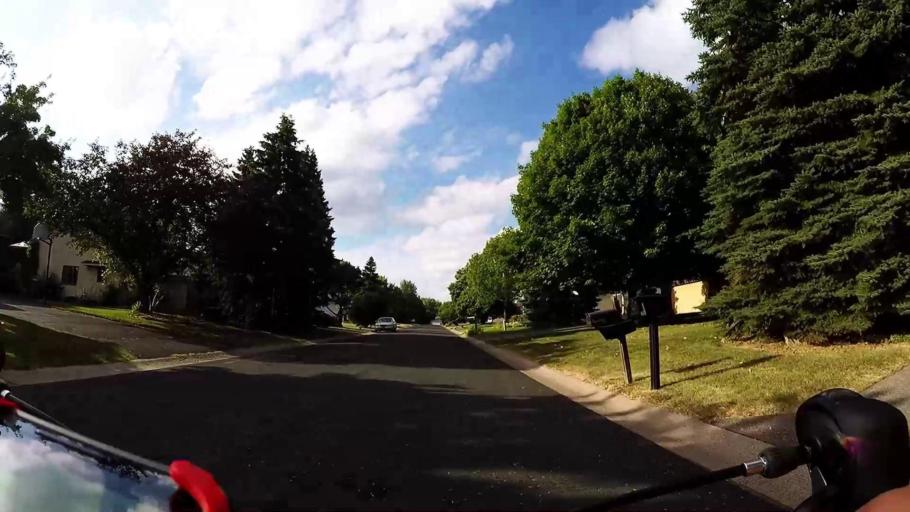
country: US
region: Minnesota
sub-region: Hennepin County
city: Minnetonka
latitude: 44.8834
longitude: -93.4940
